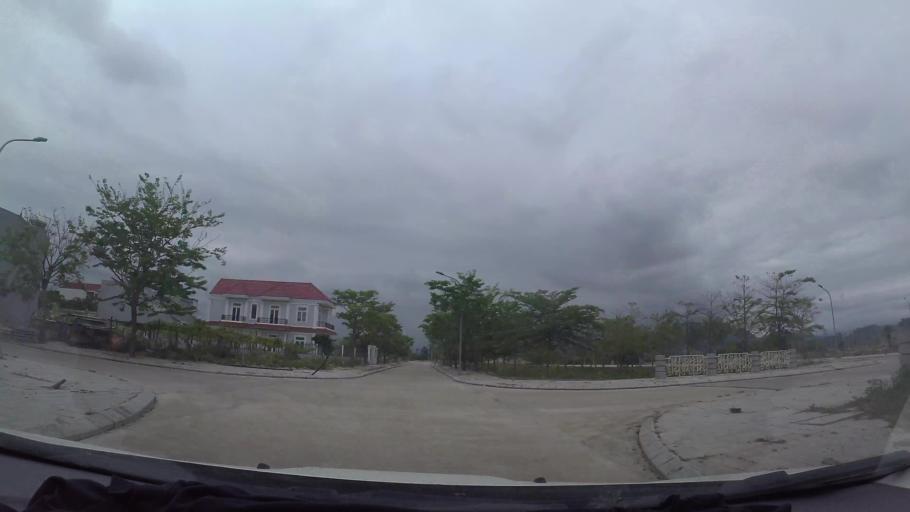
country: VN
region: Da Nang
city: Lien Chieu
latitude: 16.1036
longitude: 108.1156
